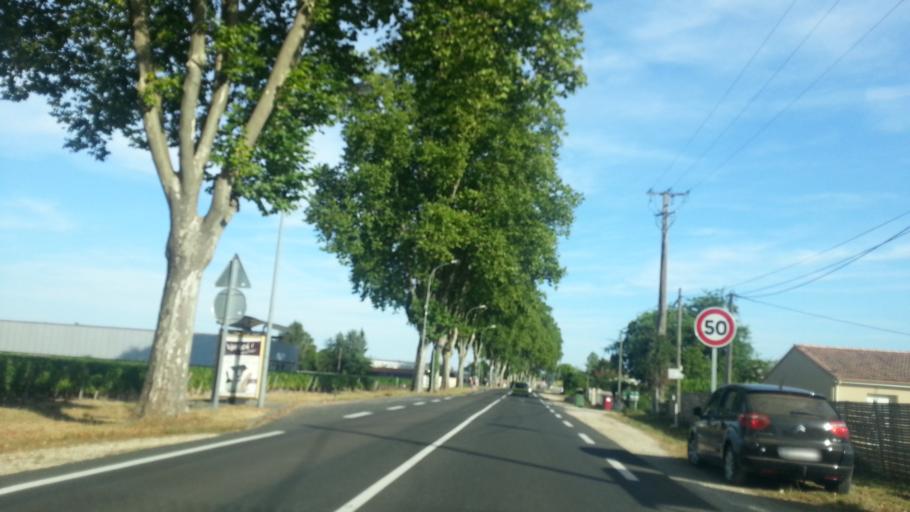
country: FR
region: Aquitaine
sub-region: Departement de la Gironde
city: Portets
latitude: 44.6780
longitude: -0.4026
